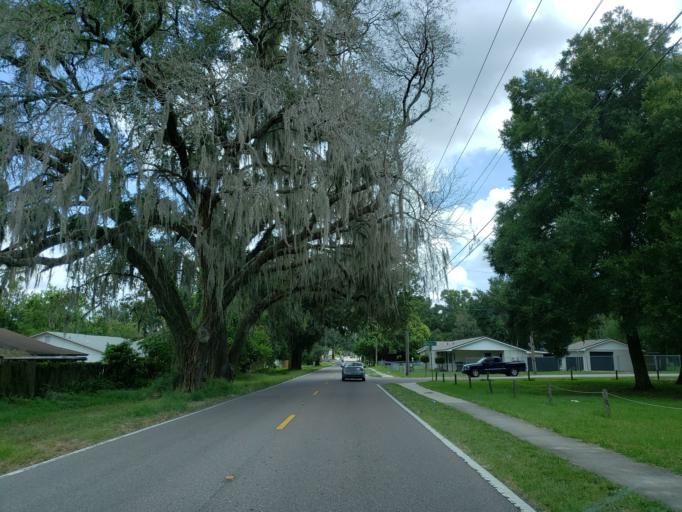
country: US
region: Florida
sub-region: Hillsborough County
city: Seffner
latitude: 27.9793
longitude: -82.2777
